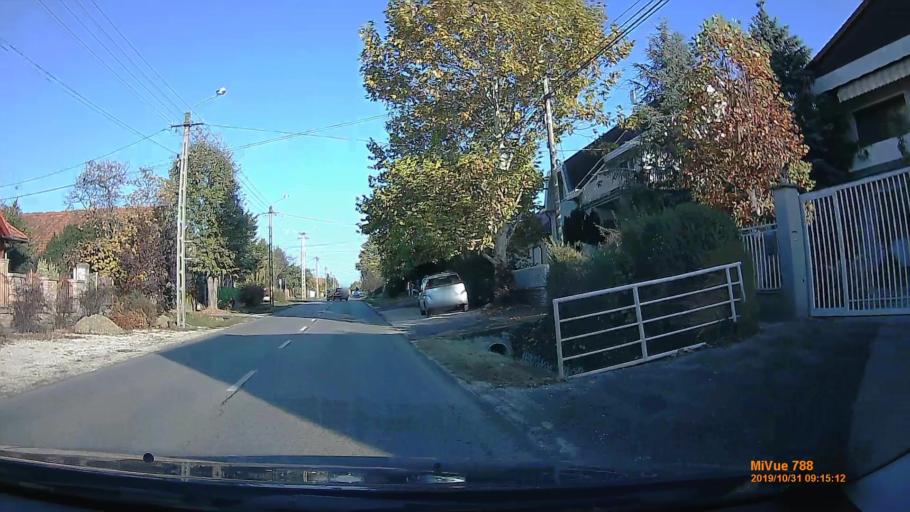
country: HU
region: Pest
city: Peteri
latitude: 47.3915
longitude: 19.4085
